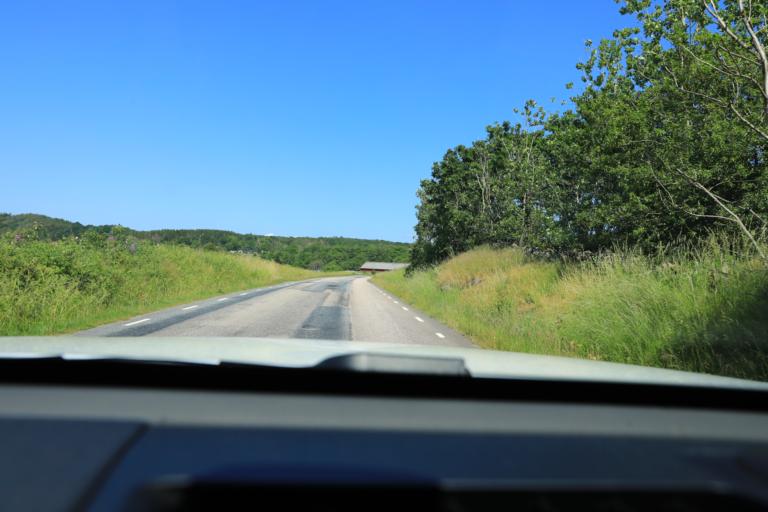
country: SE
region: Halland
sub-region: Varbergs Kommun
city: Varberg
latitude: 57.1658
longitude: 12.3186
